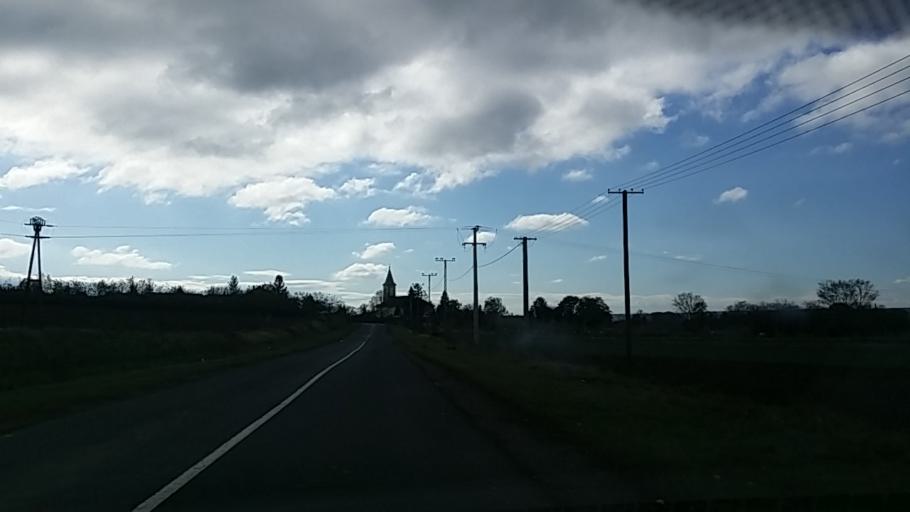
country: HU
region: Borsod-Abauj-Zemplen
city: Gonc
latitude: 48.4556
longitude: 21.2432
